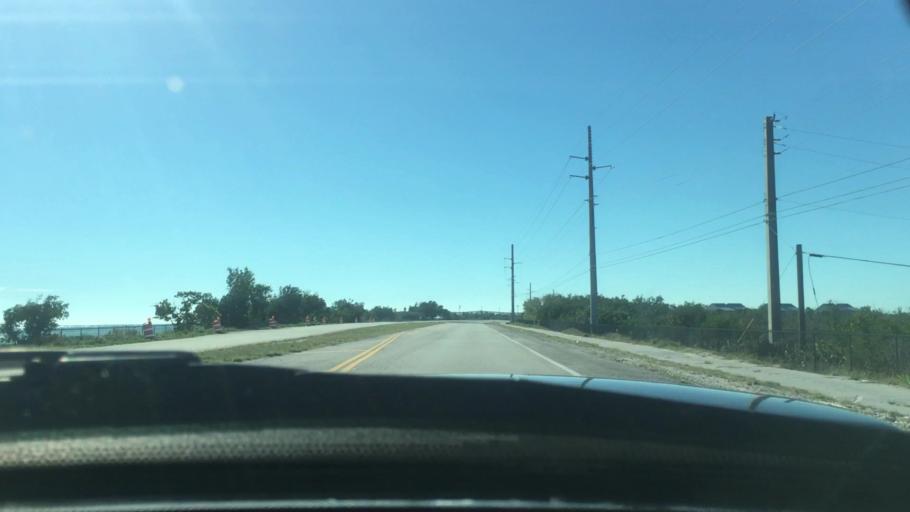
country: US
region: Florida
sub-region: Monroe County
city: Big Pine Key
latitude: 24.6618
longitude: -81.2700
